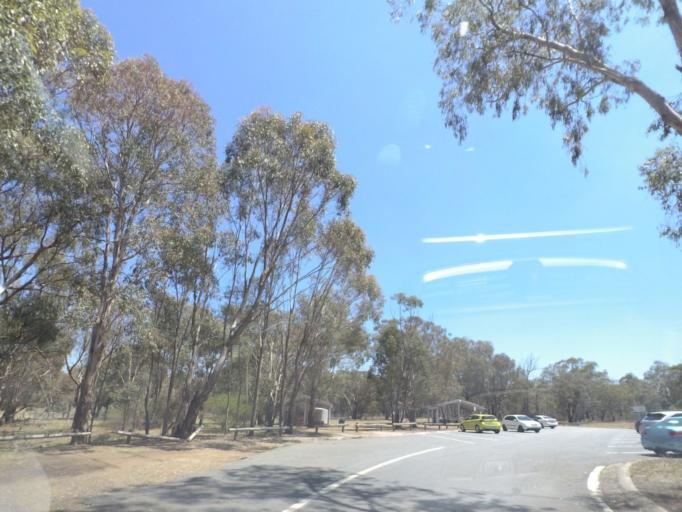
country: AU
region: Victoria
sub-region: Murrindindi
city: Kinglake West
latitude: -36.9634
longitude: 145.1808
